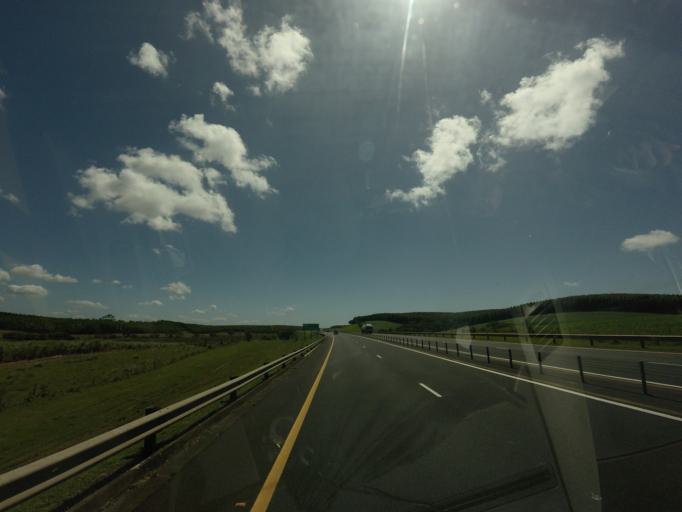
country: ZA
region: KwaZulu-Natal
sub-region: uThungulu District Municipality
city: Eshowe
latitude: -29.0475
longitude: 31.6416
